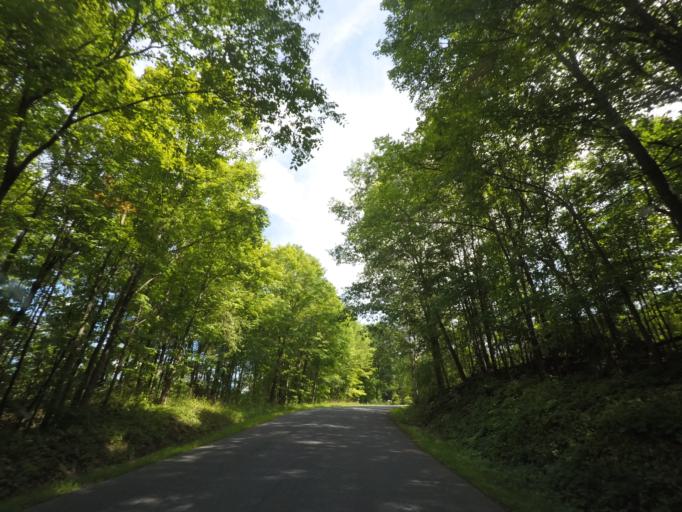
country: US
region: New York
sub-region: Rensselaer County
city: Poestenkill
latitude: 42.6883
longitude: -73.5613
